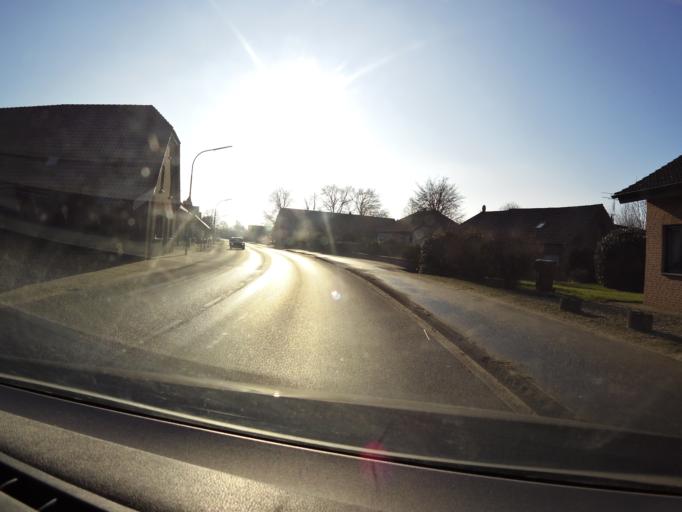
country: DE
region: North Rhine-Westphalia
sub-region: Regierungsbezirk Dusseldorf
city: Bruggen
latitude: 51.2569
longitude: 6.1842
